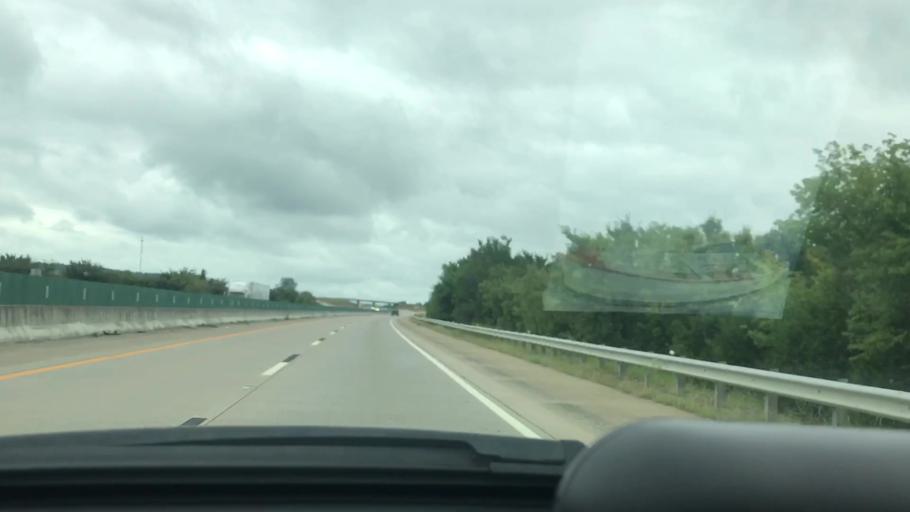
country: US
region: Oklahoma
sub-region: Pittsburg County
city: Krebs
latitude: 35.0508
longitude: -95.7091
